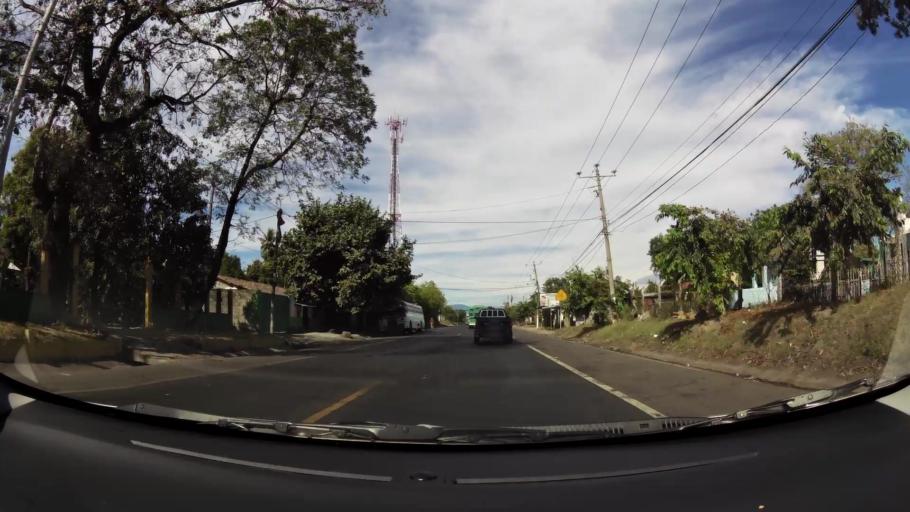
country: SV
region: San Salvador
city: Aguilares
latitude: 13.9436
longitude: -89.1895
